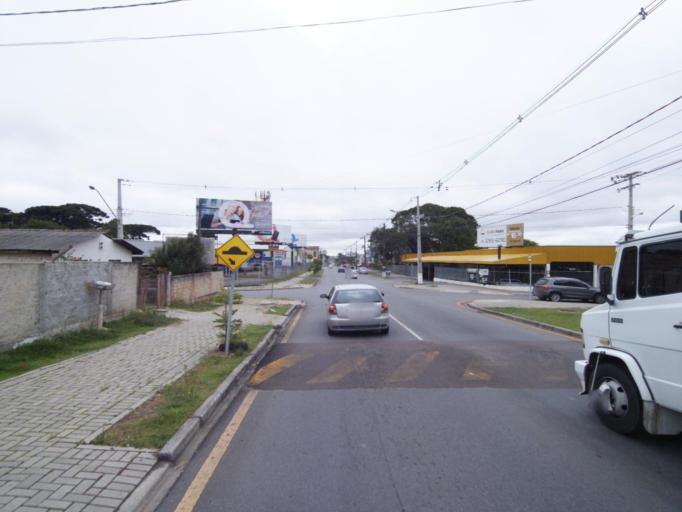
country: BR
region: Parana
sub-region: Sao Jose Dos Pinhais
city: Sao Jose dos Pinhais
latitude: -25.5352
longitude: -49.1850
